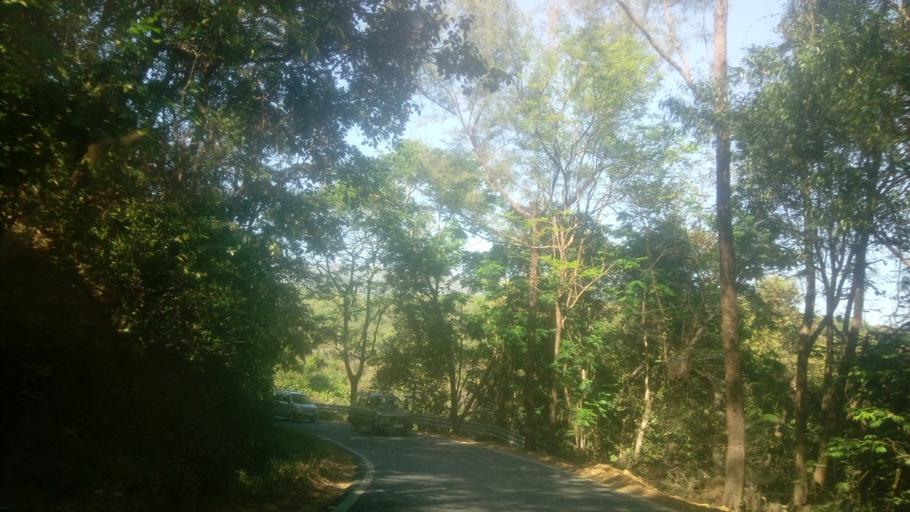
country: IN
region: Goa
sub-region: North Goa
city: Valpoy
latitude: 15.6176
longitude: 74.1202
